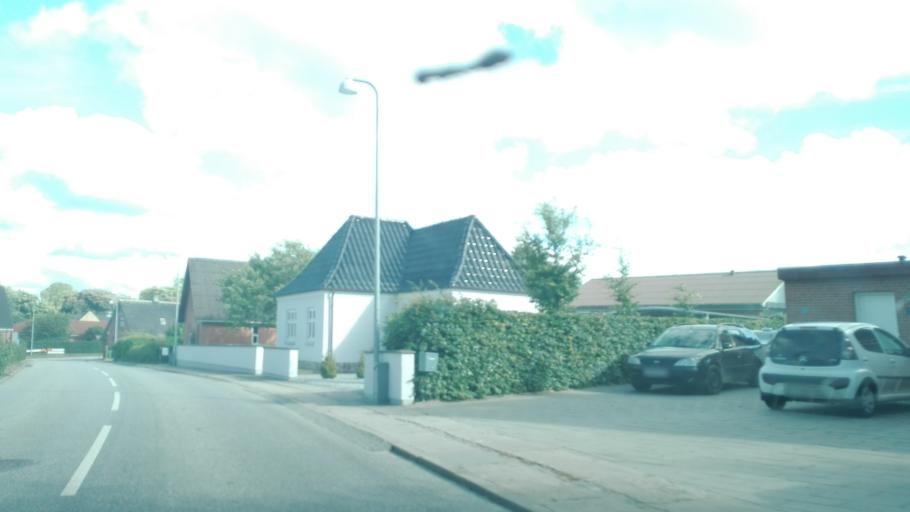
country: DK
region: Central Jutland
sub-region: Silkeborg Kommune
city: Virklund
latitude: 56.0857
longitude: 9.5693
